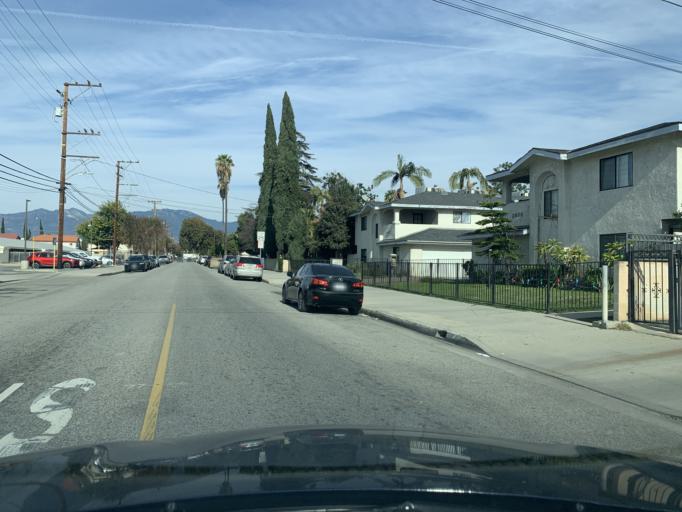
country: US
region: California
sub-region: Los Angeles County
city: South El Monte
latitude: 34.0592
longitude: -118.0557
